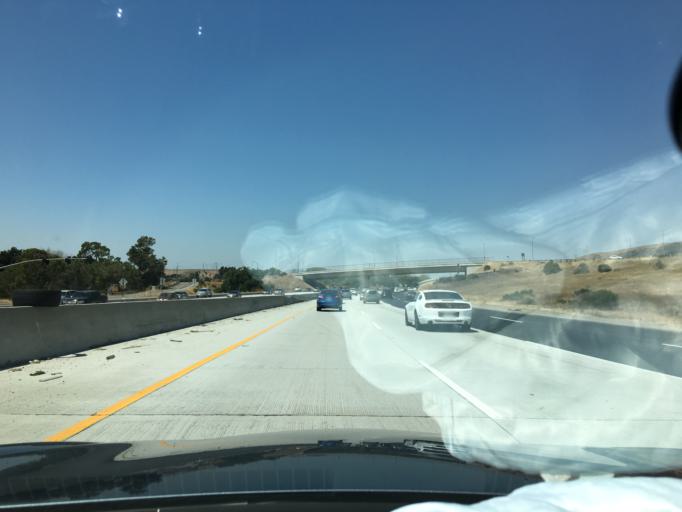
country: US
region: California
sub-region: Santa Clara County
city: Morgan Hill
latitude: 37.2078
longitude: -121.7203
